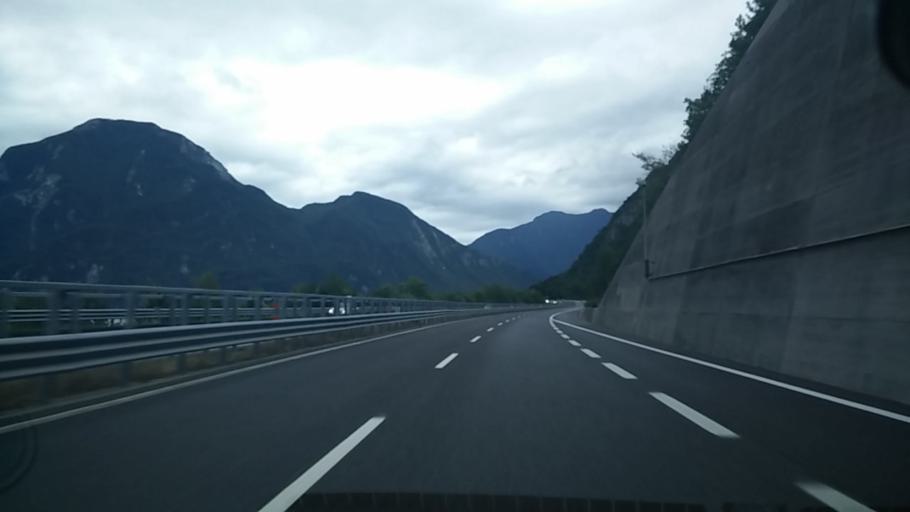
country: IT
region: Friuli Venezia Giulia
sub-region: Provincia di Udine
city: Amaro
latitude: 46.3880
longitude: 13.1288
